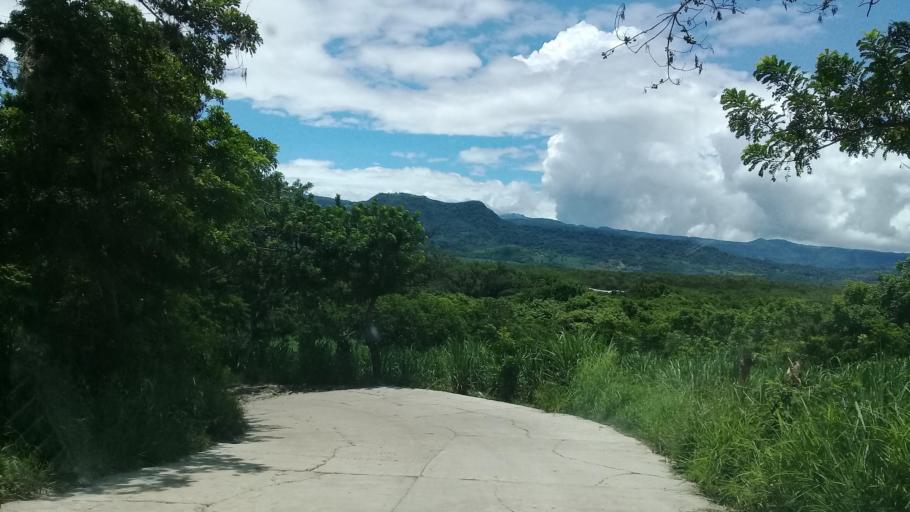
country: MX
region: Veracruz
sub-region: Naolinco
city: El Espinal
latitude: 19.5911
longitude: -96.8749
